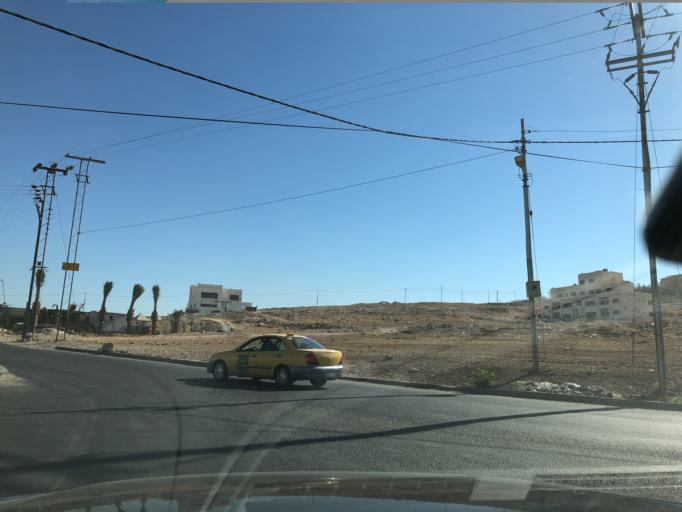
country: JO
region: Amman
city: Wadi as Sir
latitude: 31.9347
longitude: 35.8475
